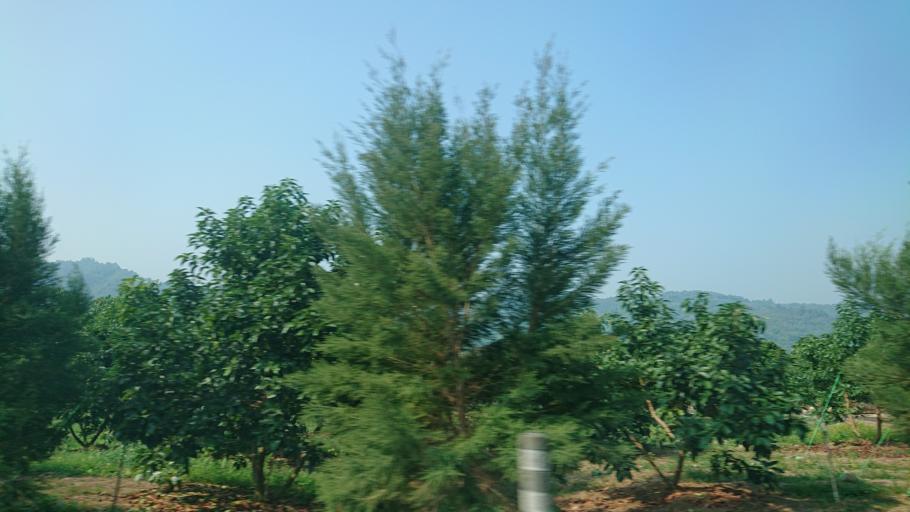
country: TW
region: Taiwan
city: Lugu
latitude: 23.6906
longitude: 120.6634
